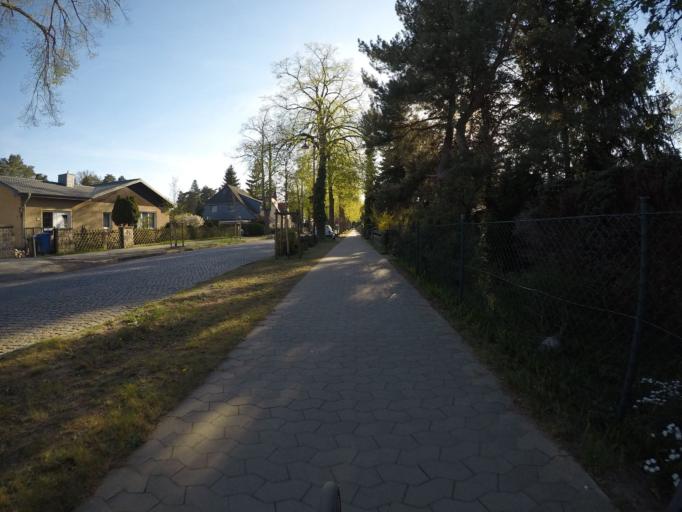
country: DE
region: Brandenburg
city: Neuenhagen
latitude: 52.5186
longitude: 13.7043
